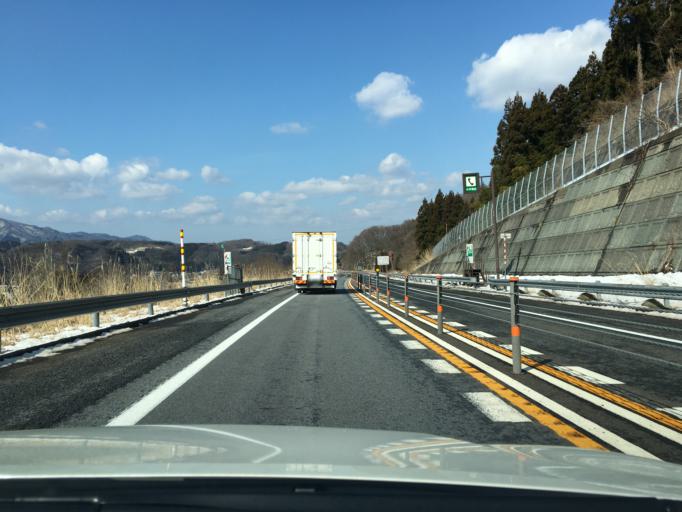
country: JP
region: Yamagata
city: Tsuruoka
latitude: 38.6055
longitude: 139.8430
